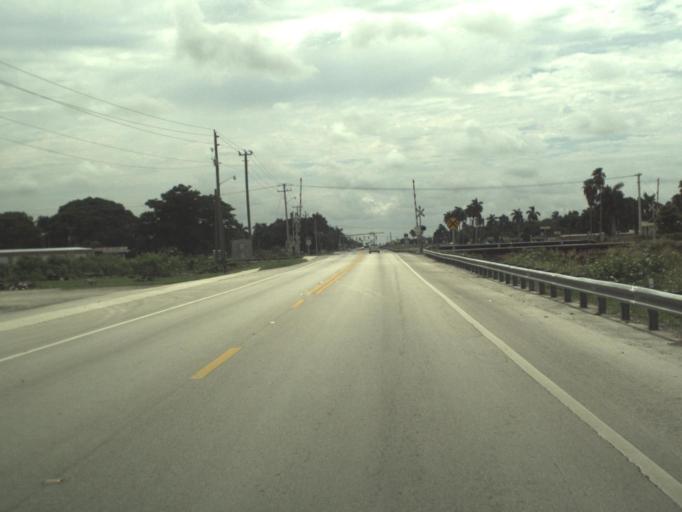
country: US
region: Florida
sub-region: Palm Beach County
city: Belle Glade
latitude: 26.6921
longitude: -80.6796
